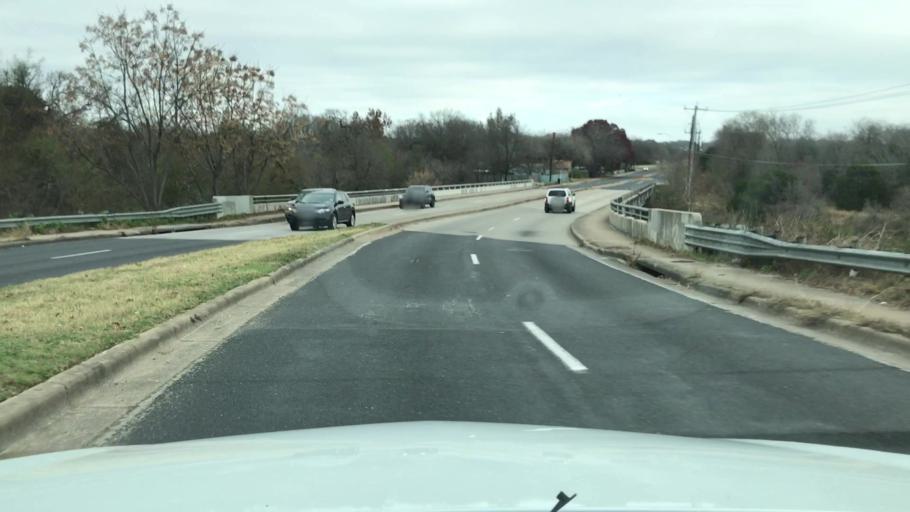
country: US
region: Texas
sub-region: Travis County
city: Onion Creek
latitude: 30.1806
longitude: -97.7467
